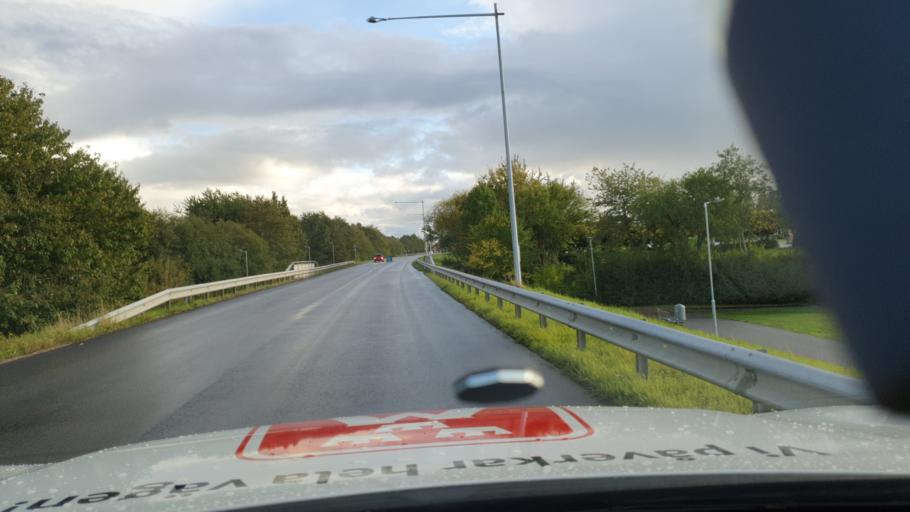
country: SE
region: Skane
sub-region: Svedala Kommun
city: Svedala
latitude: 55.5222
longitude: 13.2191
